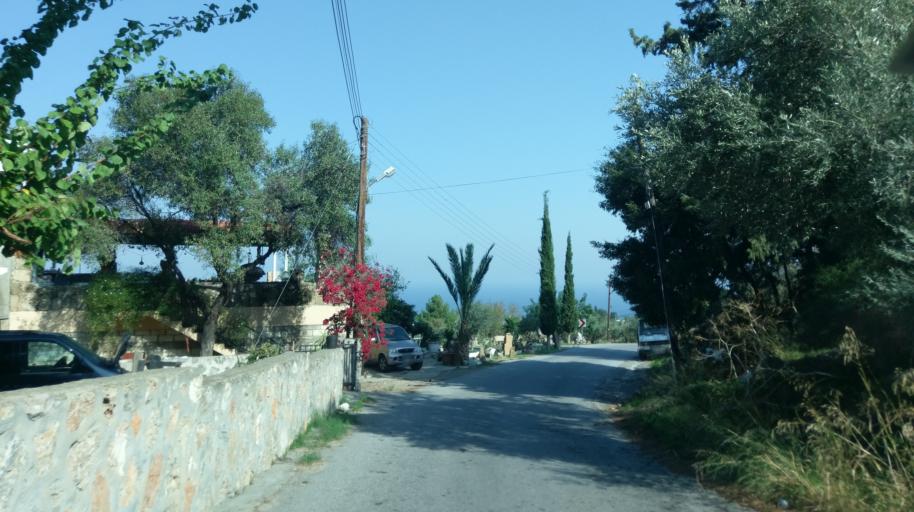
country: CY
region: Keryneia
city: Kyrenia
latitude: 35.3231
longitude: 33.2571
